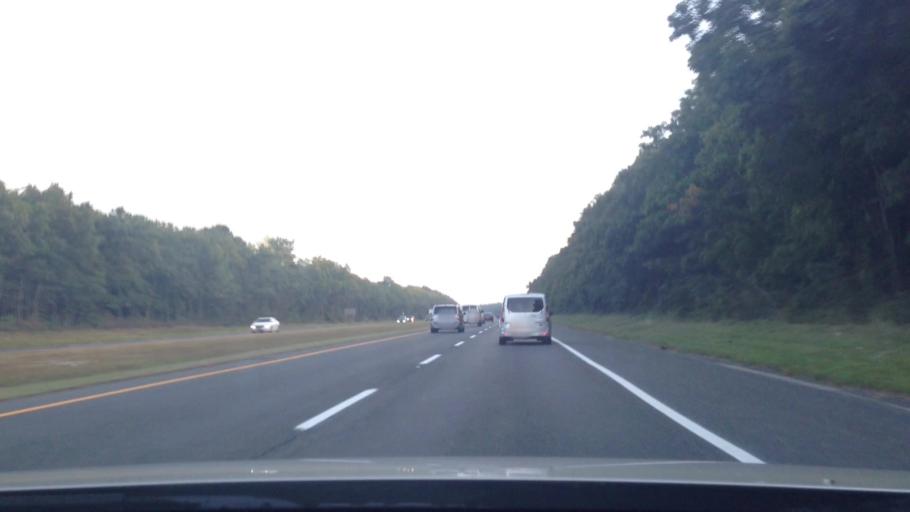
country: US
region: New York
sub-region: Suffolk County
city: Holtsville
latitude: 40.7962
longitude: -73.0514
